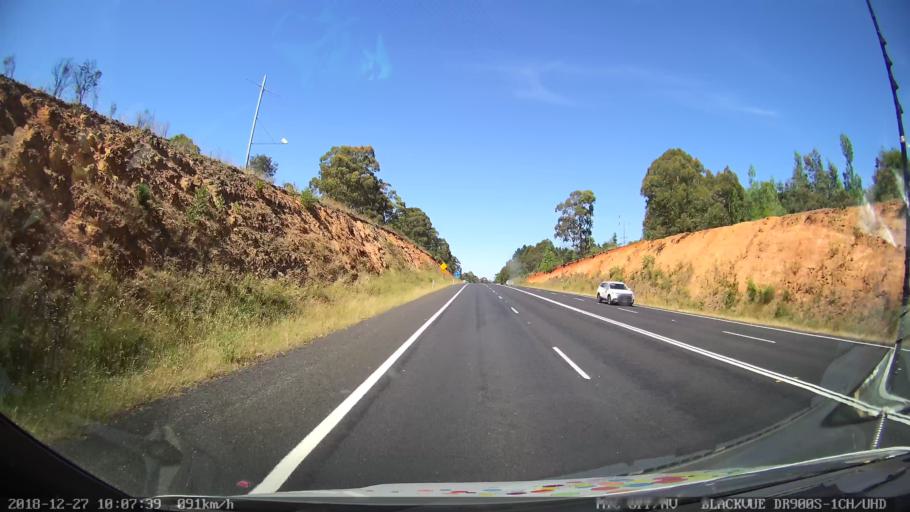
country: AU
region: New South Wales
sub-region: Lithgow
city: Portland
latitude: -33.4417
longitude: 149.8367
